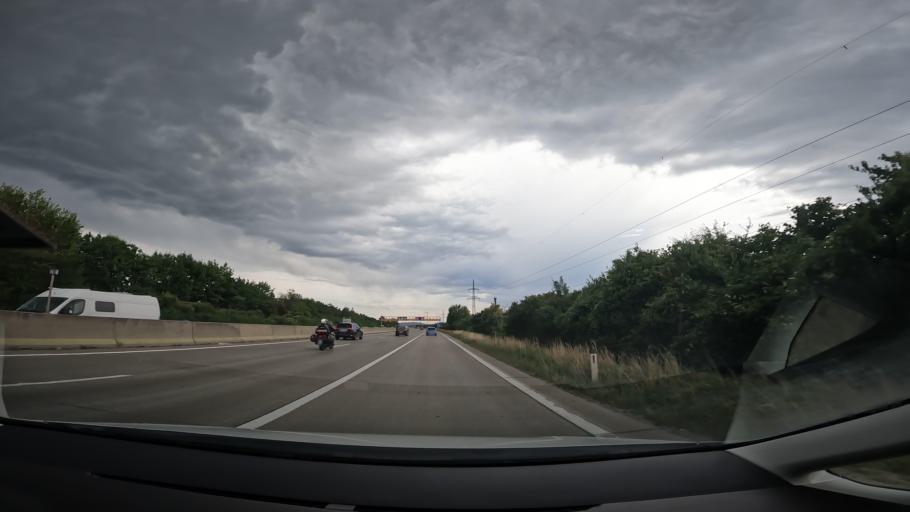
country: AT
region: Styria
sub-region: Politischer Bezirk Graz-Umgebung
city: Seiersberg
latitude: 46.9908
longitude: 15.4132
